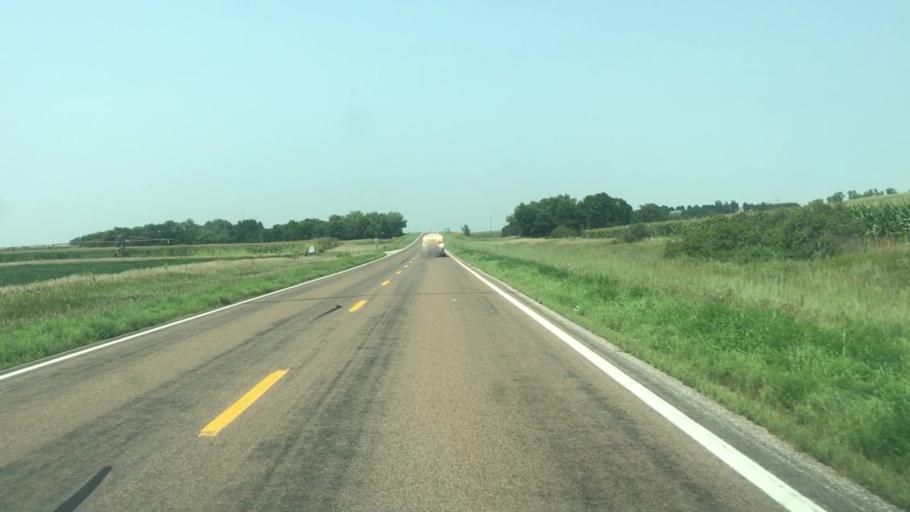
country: US
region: Nebraska
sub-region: Sherman County
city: Loup City
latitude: 41.2563
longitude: -98.9389
